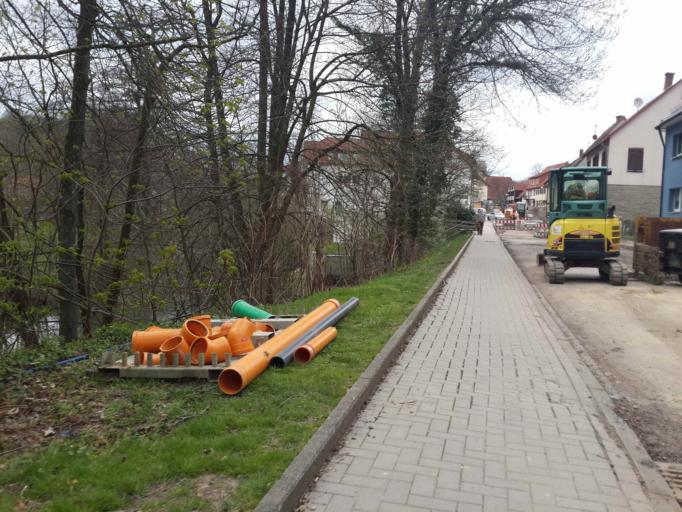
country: DE
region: Baden-Wuerttemberg
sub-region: Karlsruhe Region
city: Adelsheim
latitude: 49.3999
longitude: 9.3927
